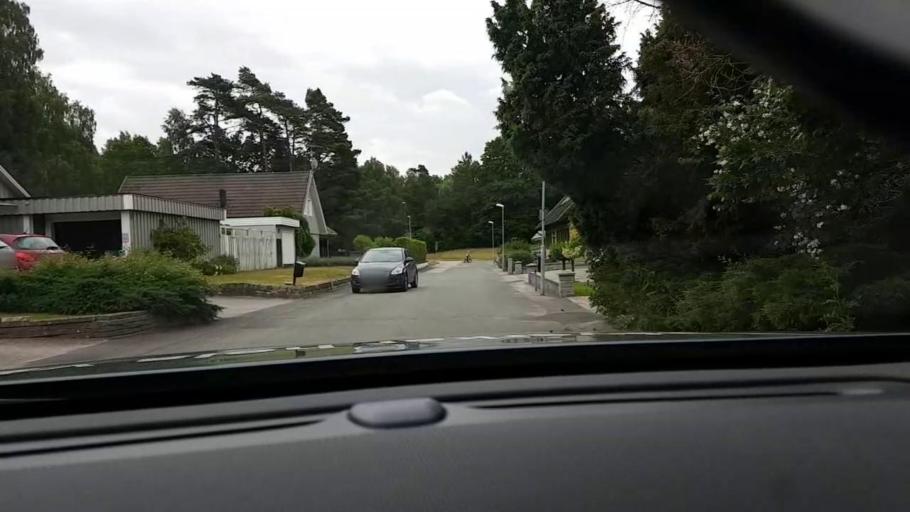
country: SE
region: Skane
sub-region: Hassleholms Kommun
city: Hassleholm
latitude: 56.1726
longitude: 13.8015
